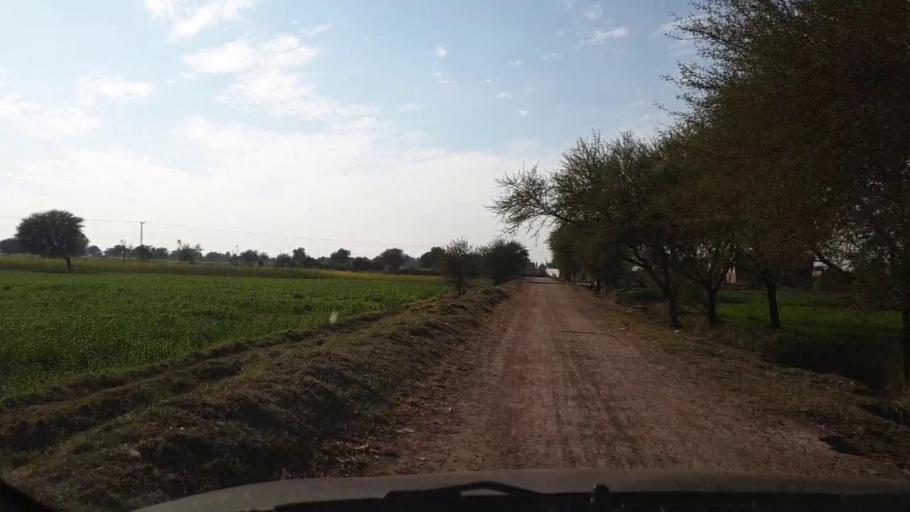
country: PK
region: Sindh
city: Jhol
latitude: 25.9768
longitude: 68.8394
